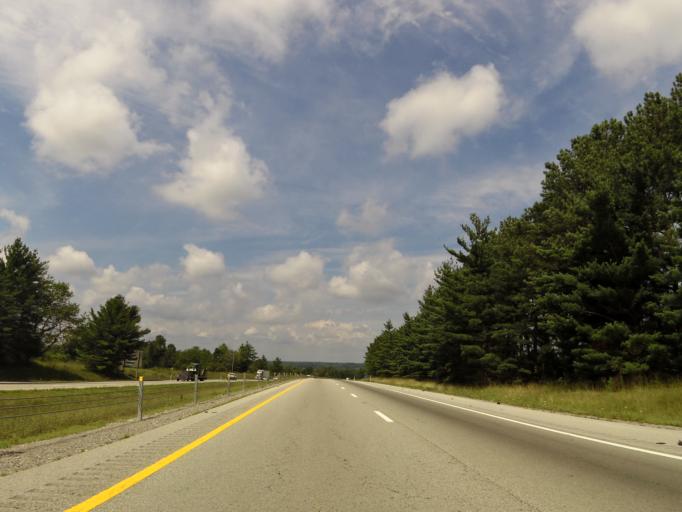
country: US
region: Tennessee
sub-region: Cumberland County
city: Fairfield Glade
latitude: 35.9148
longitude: -84.8996
